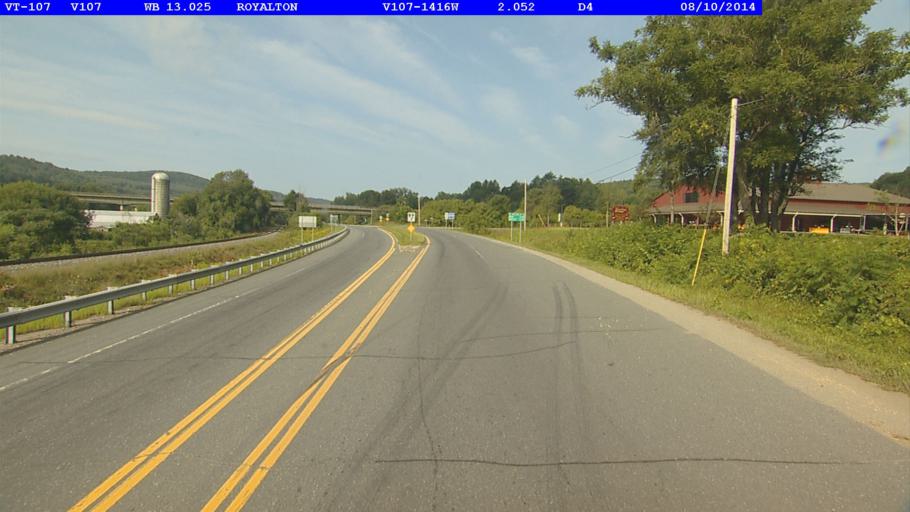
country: US
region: Vermont
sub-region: Orange County
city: Randolph
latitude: 43.8275
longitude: -72.5758
